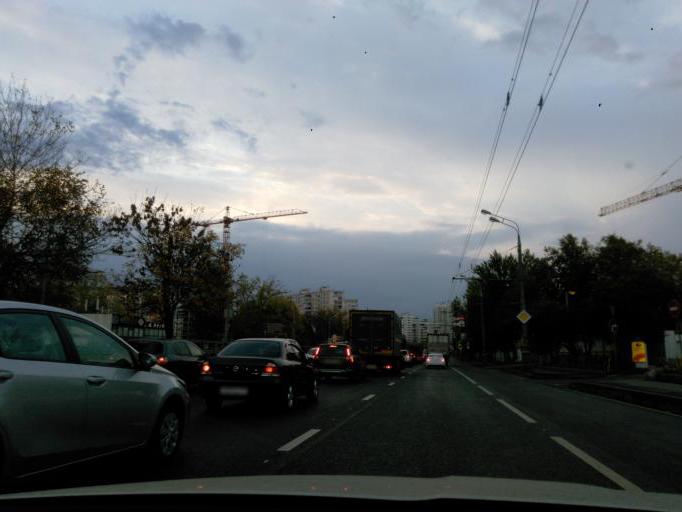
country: RU
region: Moscow
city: Likhobory
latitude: 55.8597
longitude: 37.5554
